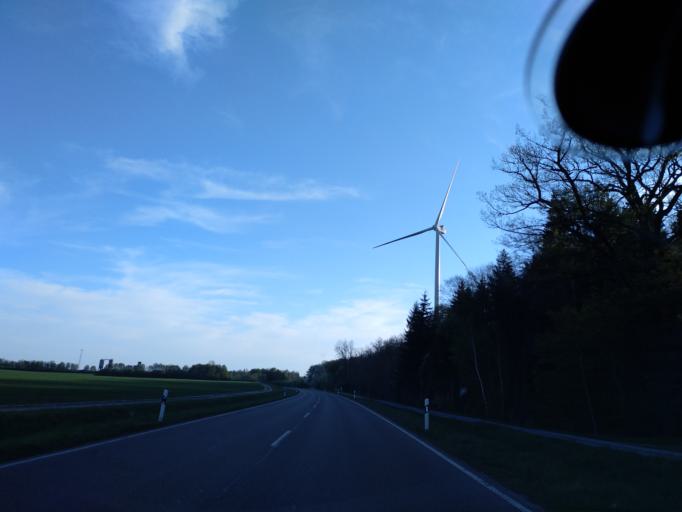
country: DE
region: Baden-Wuerttemberg
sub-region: Regierungsbezirk Stuttgart
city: Kirchberg an der Jagst
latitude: 49.1846
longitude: 9.9644
